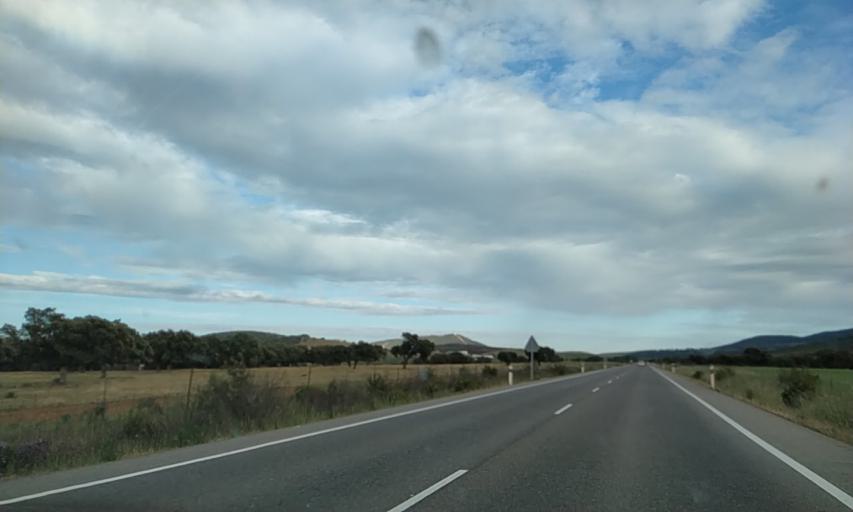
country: ES
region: Extremadura
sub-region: Provincia de Caceres
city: Pedroso de Acim
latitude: 39.8595
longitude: -6.4276
